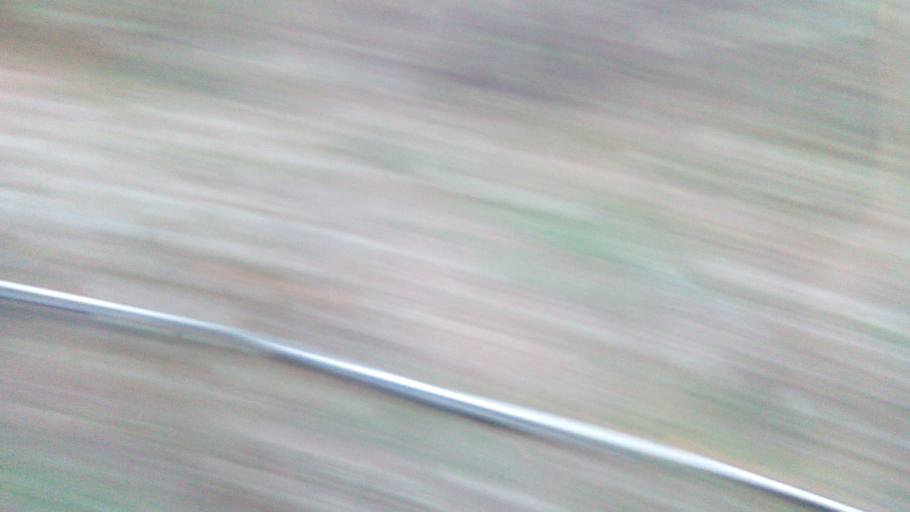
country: TW
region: Taiwan
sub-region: Hualien
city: Hualian
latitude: 24.3419
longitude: 121.3154
